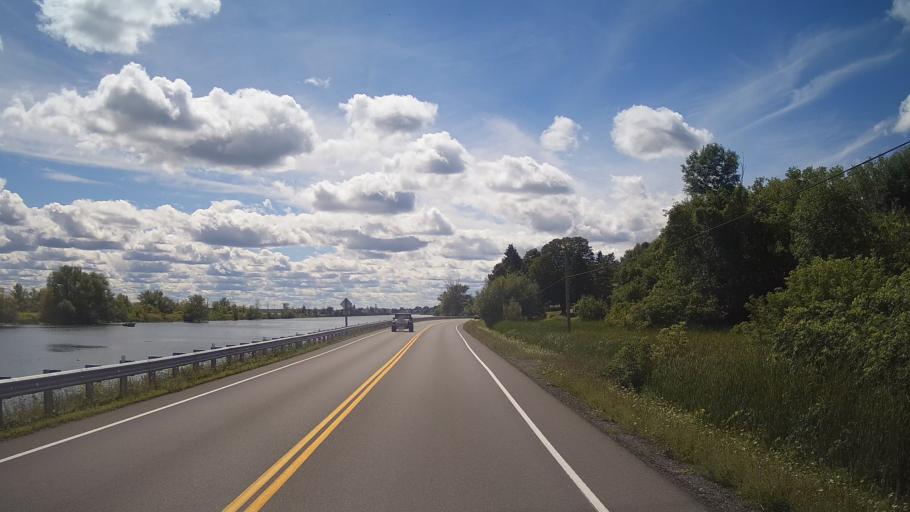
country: US
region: New York
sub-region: St. Lawrence County
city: Ogdensburg
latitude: 44.8135
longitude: -75.3448
